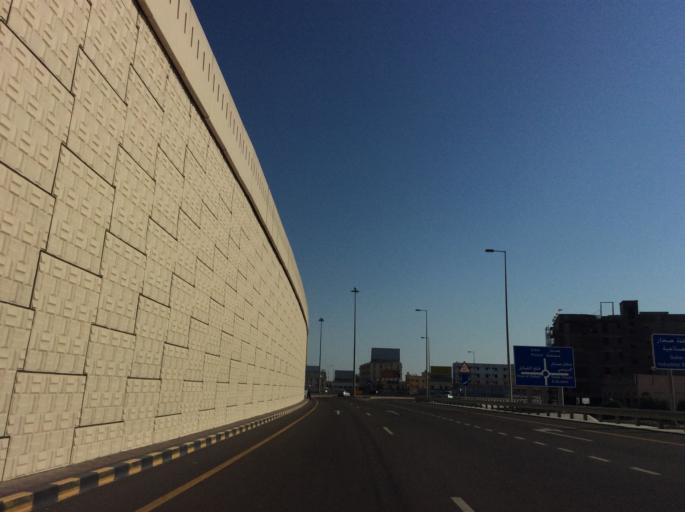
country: OM
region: Al Batinah
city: Al Liwa'
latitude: 24.4260
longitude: 56.6093
